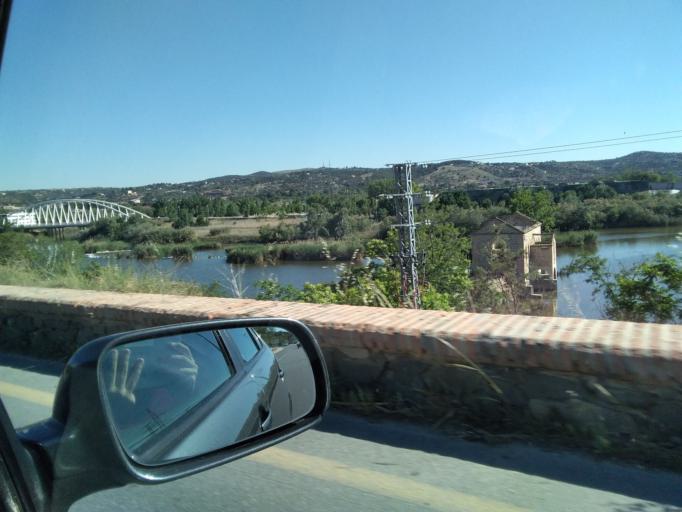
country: ES
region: Castille-La Mancha
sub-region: Province of Toledo
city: Toledo
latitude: 39.8781
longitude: -4.0461
